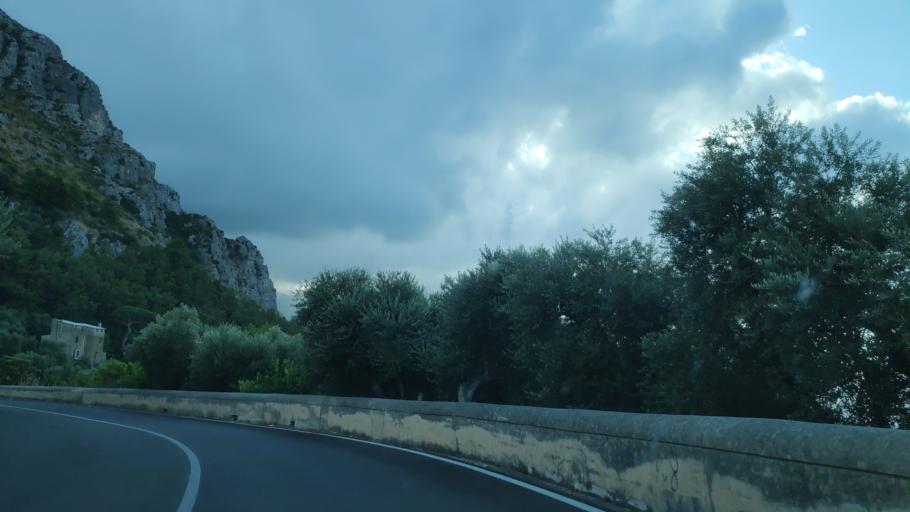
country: IT
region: Campania
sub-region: Provincia di Napoli
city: Arola-Preazzano
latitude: 40.6161
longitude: 14.4324
